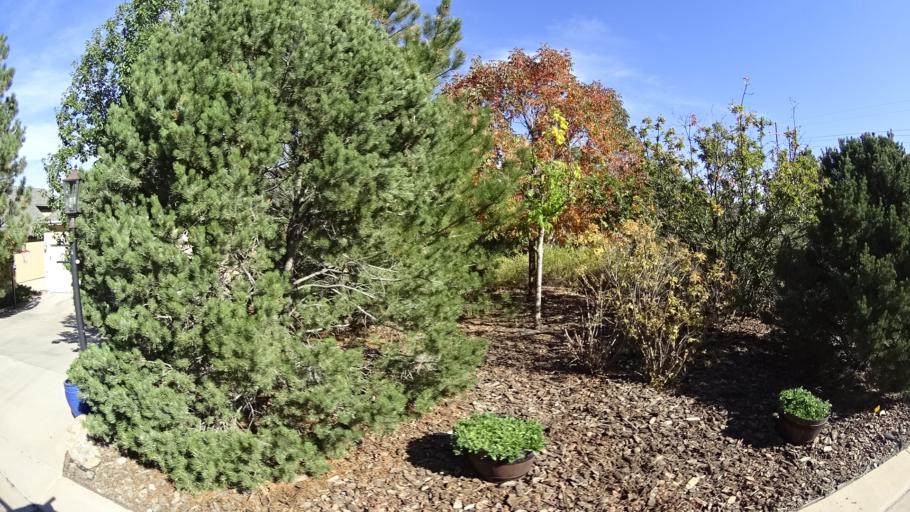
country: US
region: Colorado
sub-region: El Paso County
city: Colorado Springs
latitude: 38.9091
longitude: -104.7899
